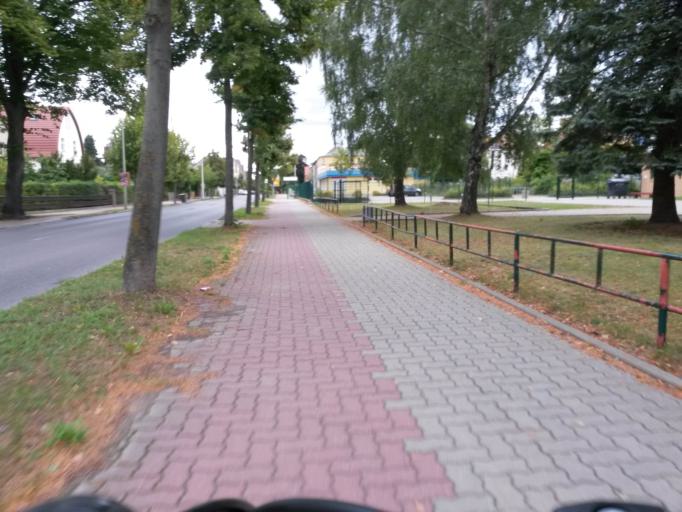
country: DE
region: Brandenburg
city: Angermunde
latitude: 53.0111
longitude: 13.9942
